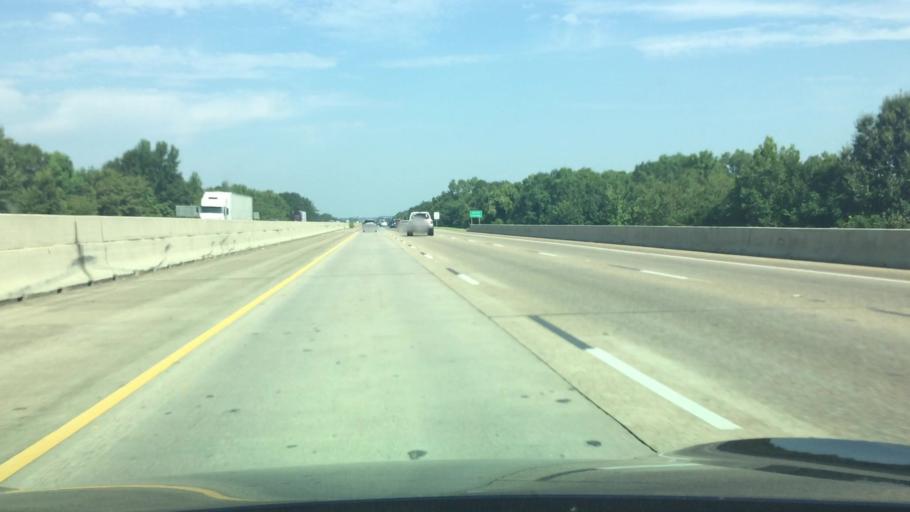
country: US
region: Alabama
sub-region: Montgomery County
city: Montgomery
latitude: 32.3946
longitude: -86.3292
